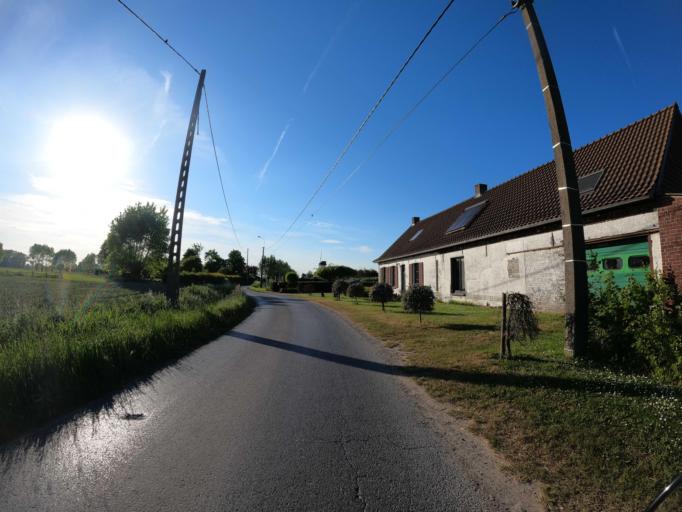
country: BE
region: Flanders
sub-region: Provincie West-Vlaanderen
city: Ruiselede
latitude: 51.0189
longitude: 3.4423
